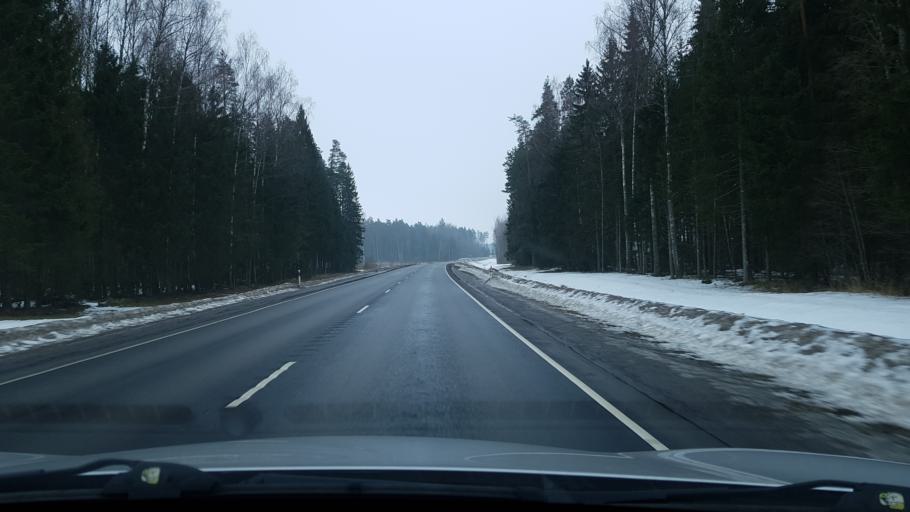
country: EE
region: Valgamaa
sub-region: Valga linn
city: Valga
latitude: 57.8886
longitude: 26.1654
